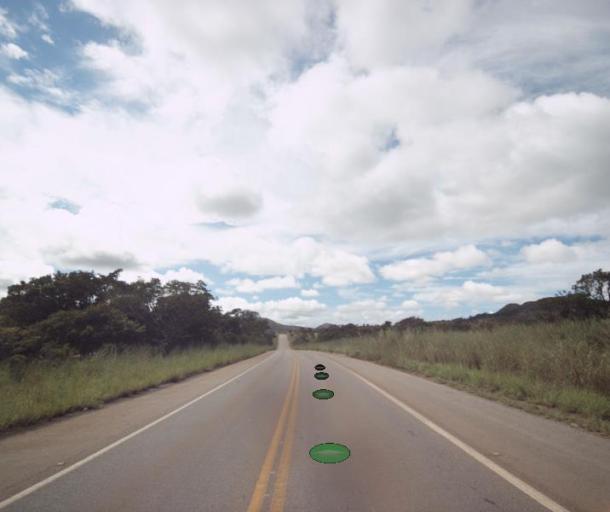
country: BR
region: Goias
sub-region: Barro Alto
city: Barro Alto
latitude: -15.1448
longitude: -48.8180
